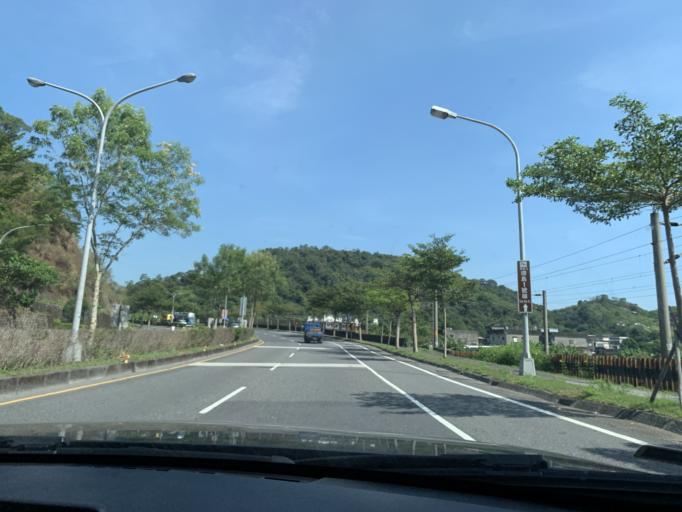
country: TW
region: Taiwan
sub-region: Yilan
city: Yilan
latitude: 24.6024
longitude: 121.8347
